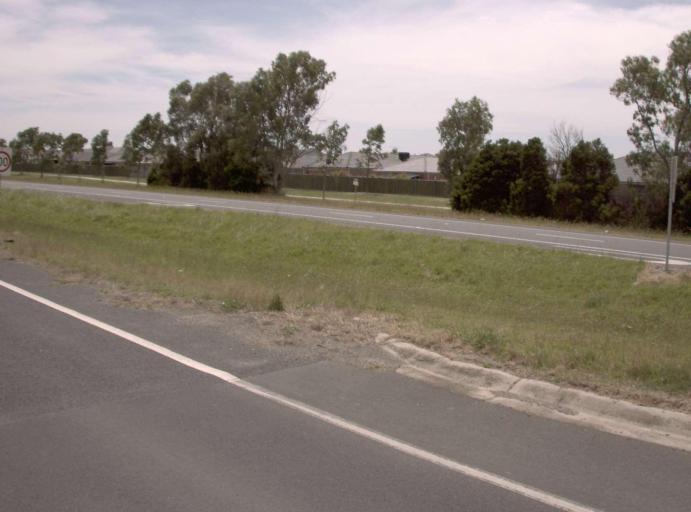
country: AU
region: Victoria
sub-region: Casey
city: Lynbrook
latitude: -38.0700
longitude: 145.2408
